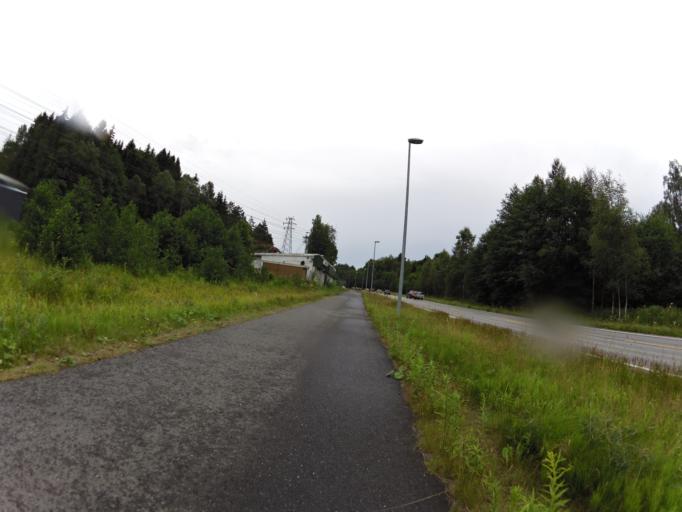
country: NO
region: Ostfold
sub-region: Moss
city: Moss
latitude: 59.4598
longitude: 10.6874
